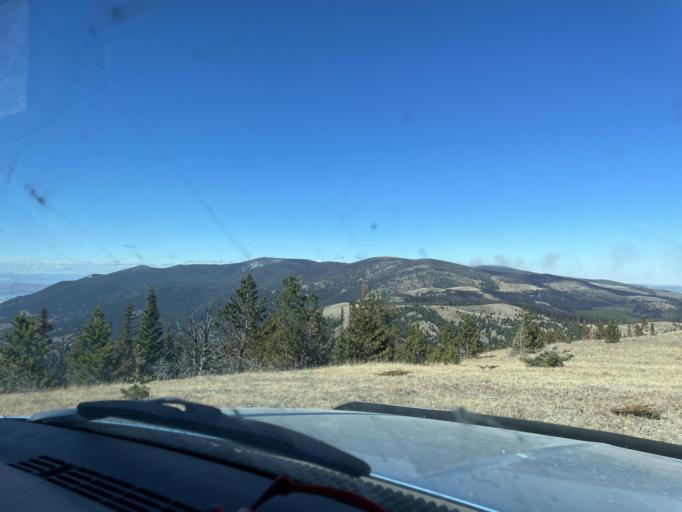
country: US
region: Montana
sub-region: Broadwater County
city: Townsend
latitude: 46.4848
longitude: -111.2547
